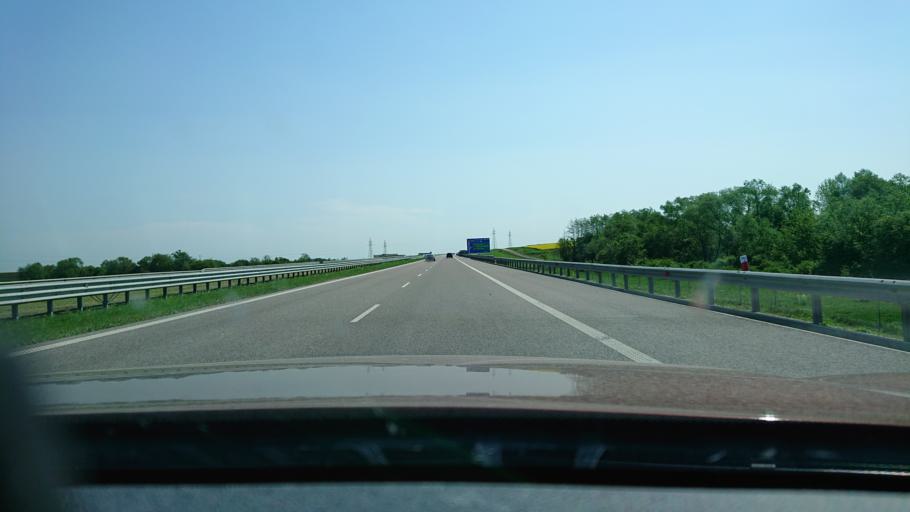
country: PL
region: Subcarpathian Voivodeship
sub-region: Powiat przemyski
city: Orly
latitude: 49.9152
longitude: 22.7789
